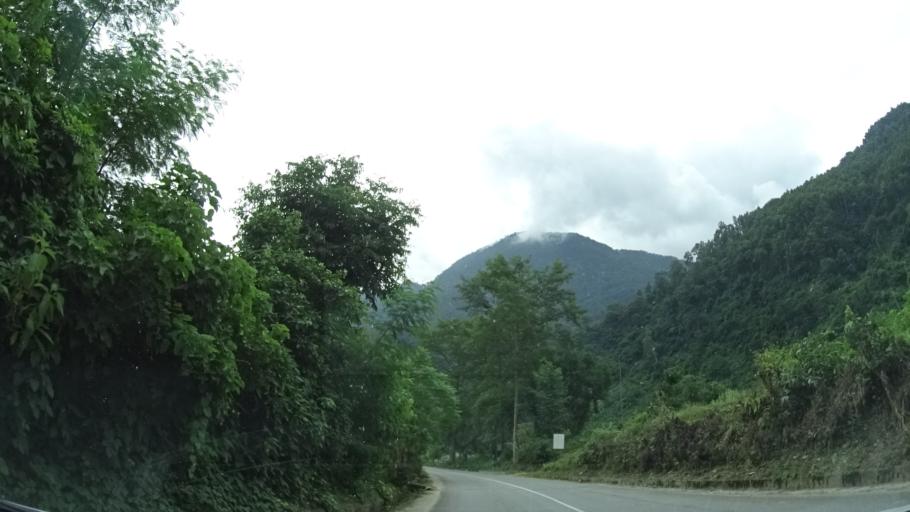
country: NP
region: Central Region
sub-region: Narayani Zone
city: Bharatpur
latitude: 27.9152
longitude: 84.4988
